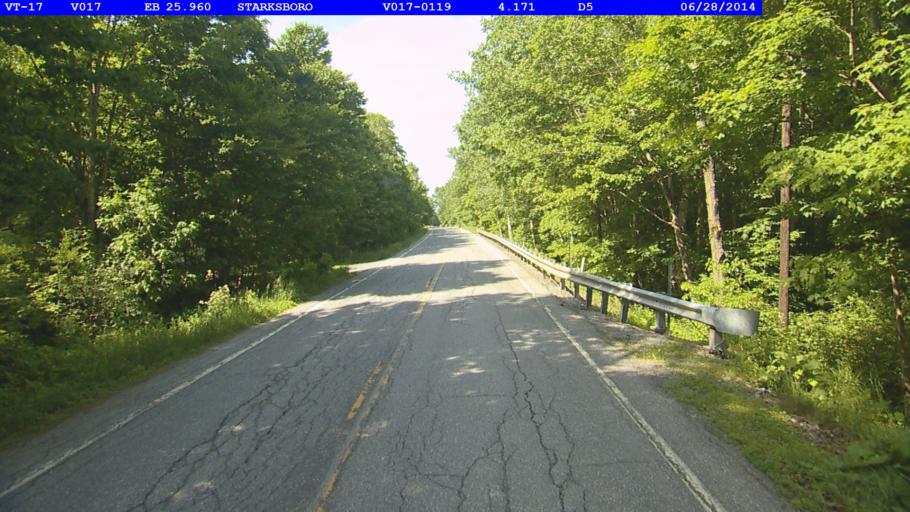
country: US
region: Vermont
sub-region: Addison County
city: Bristol
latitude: 44.1992
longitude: -72.9650
